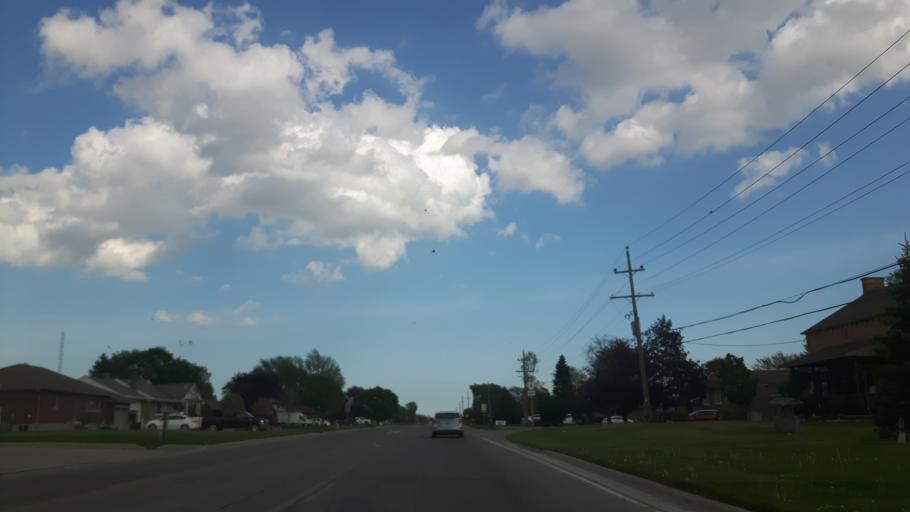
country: CA
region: Ontario
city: South Huron
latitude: 43.1847
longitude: -81.3961
